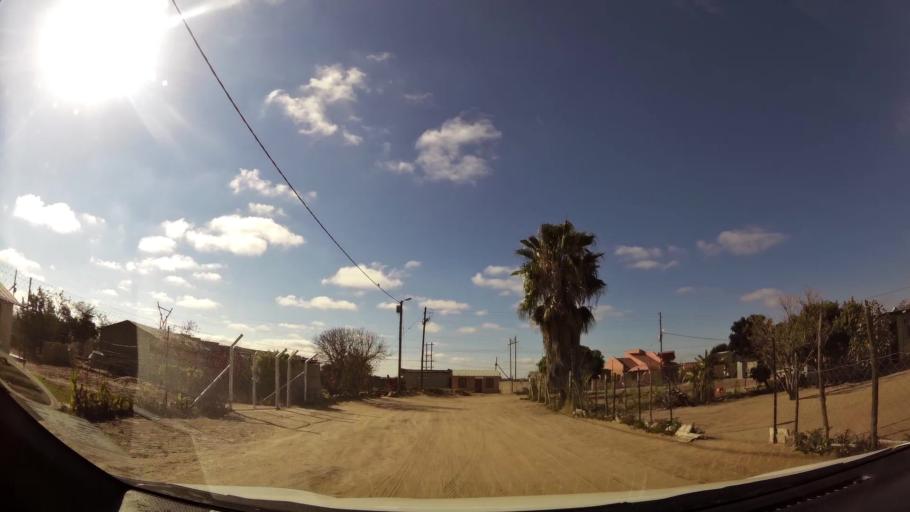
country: ZA
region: Limpopo
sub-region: Capricorn District Municipality
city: Polokwane
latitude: -23.8448
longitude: 29.4050
